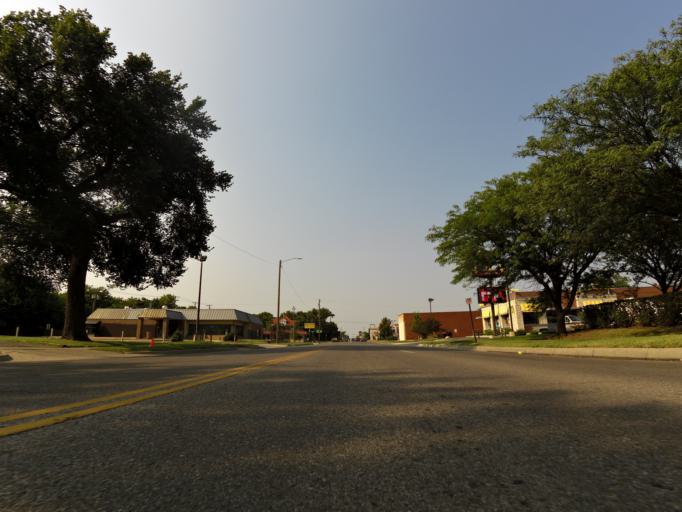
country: US
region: Kansas
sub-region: Sedgwick County
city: Wichita
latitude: 37.7016
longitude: -97.3356
